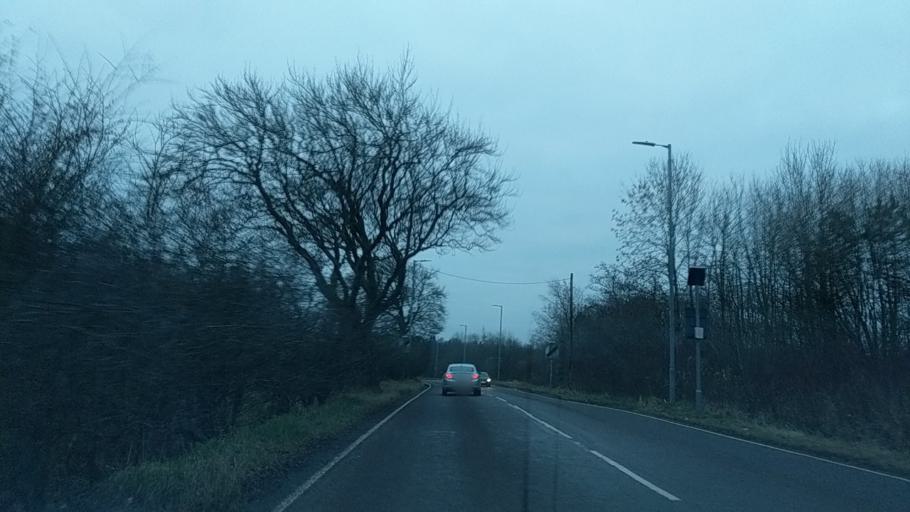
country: GB
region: Scotland
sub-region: South Lanarkshire
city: East Kilbride
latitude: 55.7419
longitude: -4.1578
